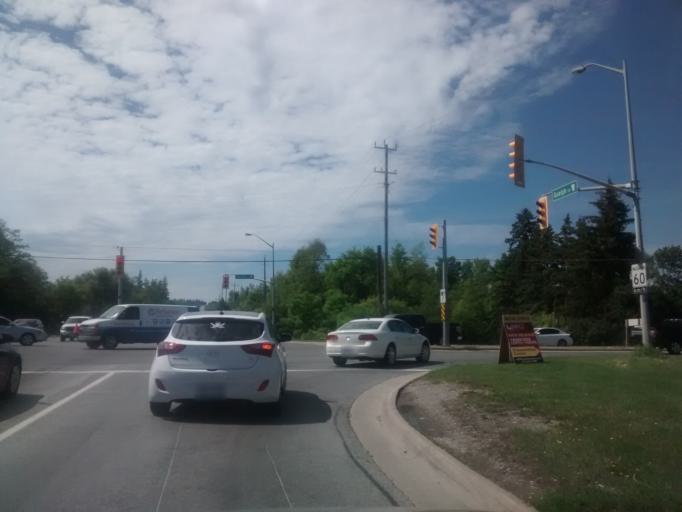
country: CA
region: Ontario
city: Burlington
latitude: 43.3776
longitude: -79.8394
